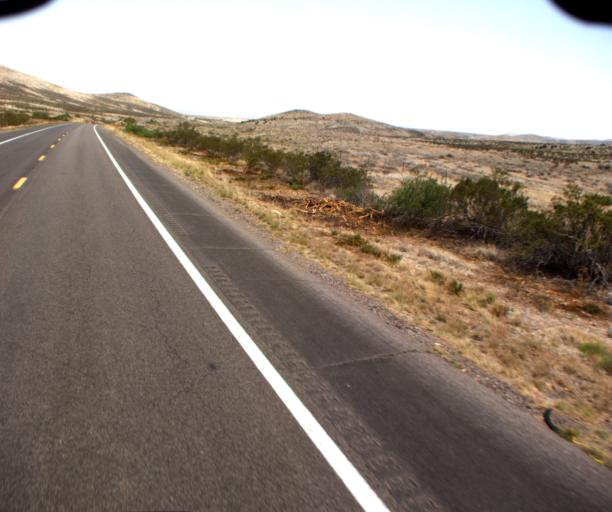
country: US
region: Arizona
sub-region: Greenlee County
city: Clifton
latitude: 32.7438
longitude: -109.2141
